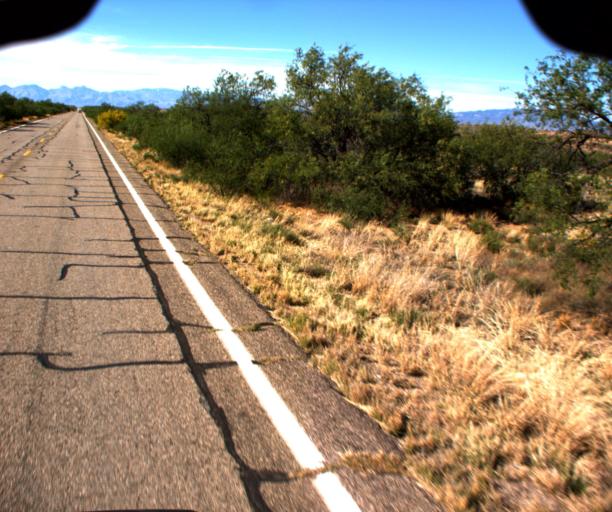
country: US
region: Arizona
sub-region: Pima County
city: Vail
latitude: 31.9573
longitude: -110.6696
